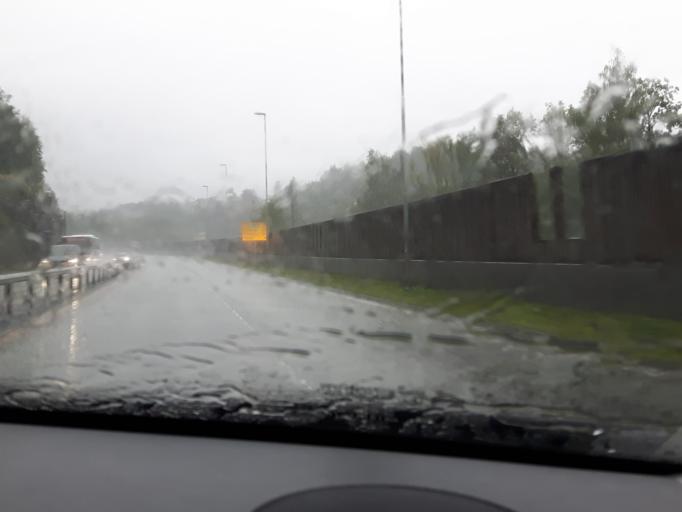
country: NO
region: Vest-Agder
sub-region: Kristiansand
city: Kristiansand
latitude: 58.1394
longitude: 7.9442
